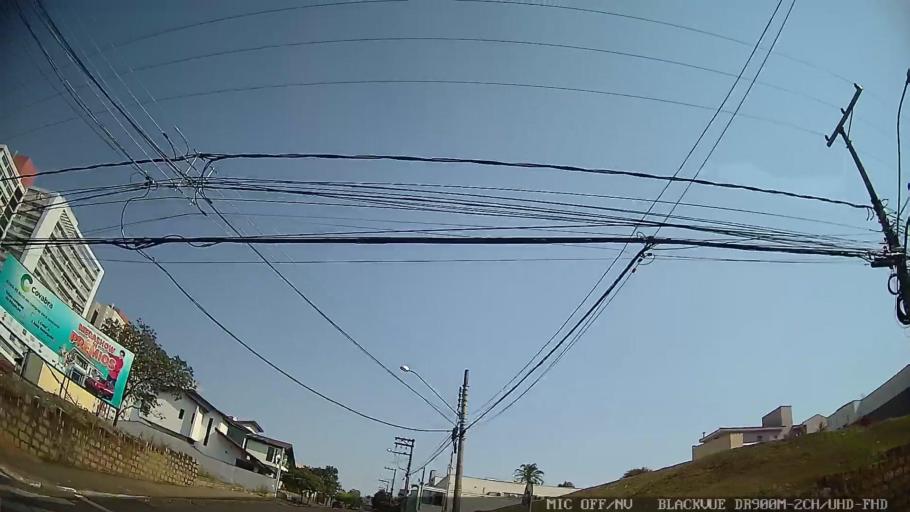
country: BR
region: Sao Paulo
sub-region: Itatiba
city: Itatiba
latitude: -23.0056
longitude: -46.8493
